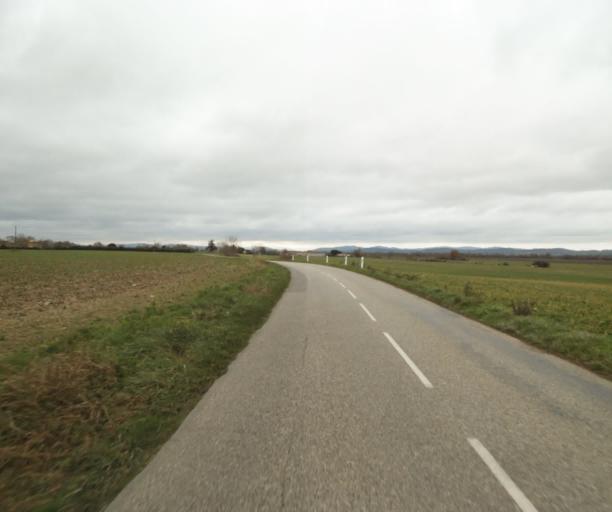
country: FR
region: Midi-Pyrenees
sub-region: Departement de l'Ariege
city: Pamiers
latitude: 43.1713
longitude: 1.6353
